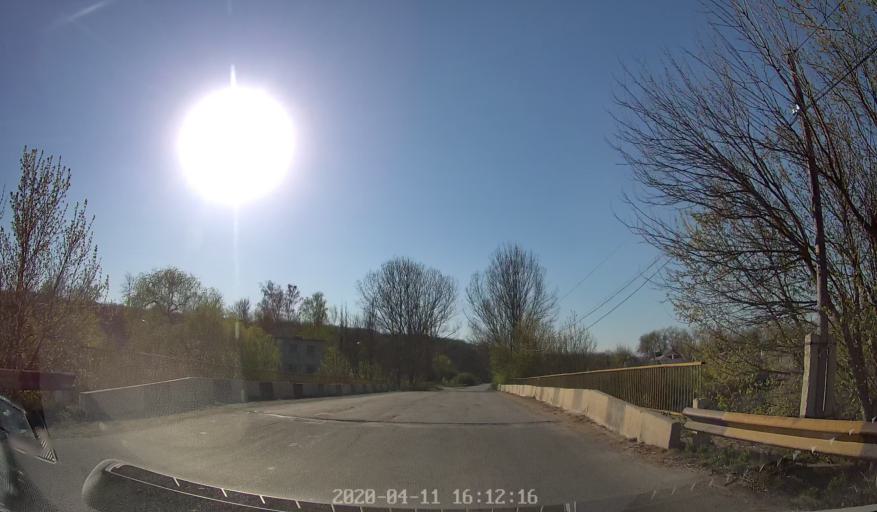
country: MD
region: Chisinau
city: Vadul lui Voda
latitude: 47.0693
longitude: 29.1235
